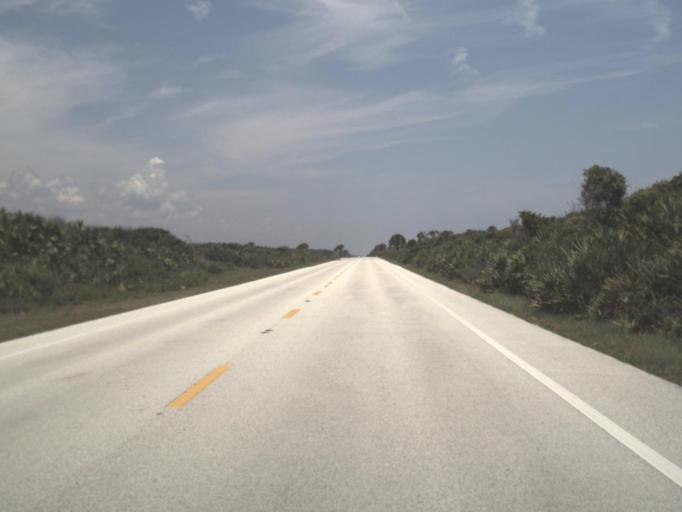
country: US
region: Florida
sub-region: Saint Johns County
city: Palm Valley
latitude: 30.1074
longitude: -81.3434
